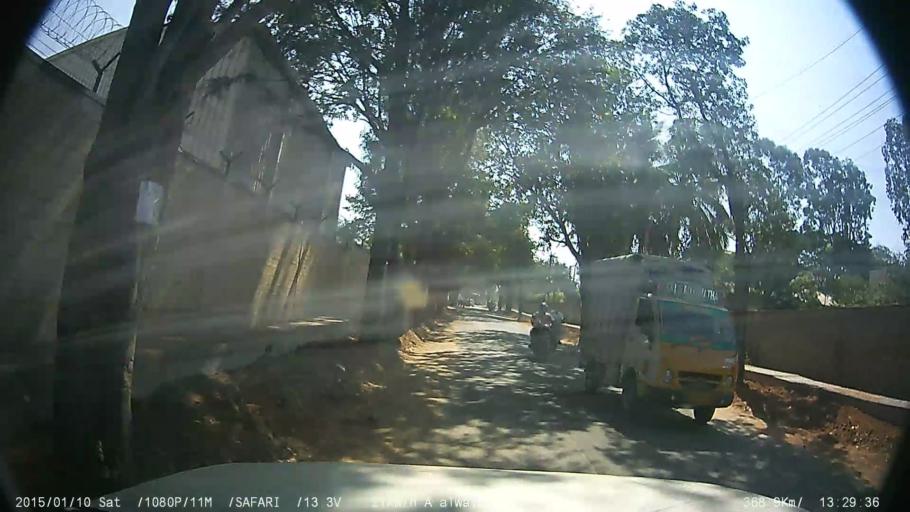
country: IN
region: Tamil Nadu
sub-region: Krishnagiri
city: Hosur
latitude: 12.7693
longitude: 77.7970
